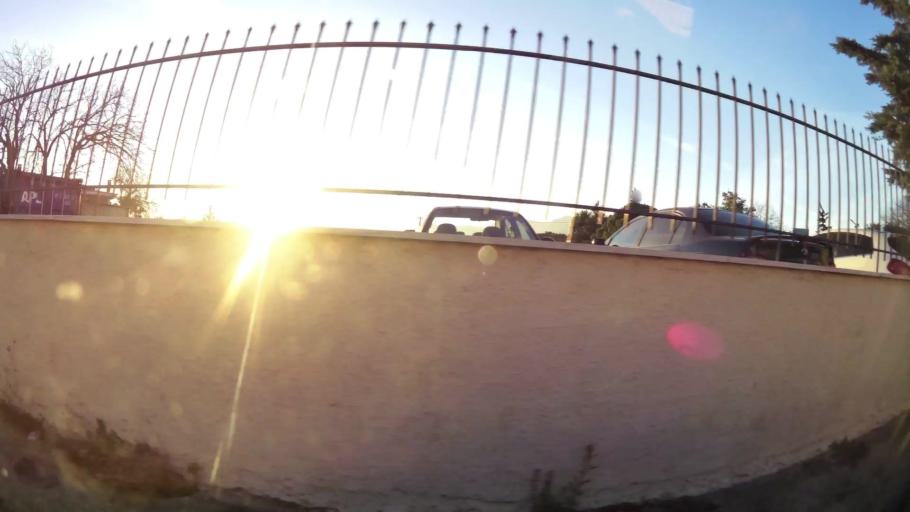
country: GR
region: Attica
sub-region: Nomarchia Anatolikis Attikis
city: Kryoneri
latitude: 38.1280
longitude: 23.8351
